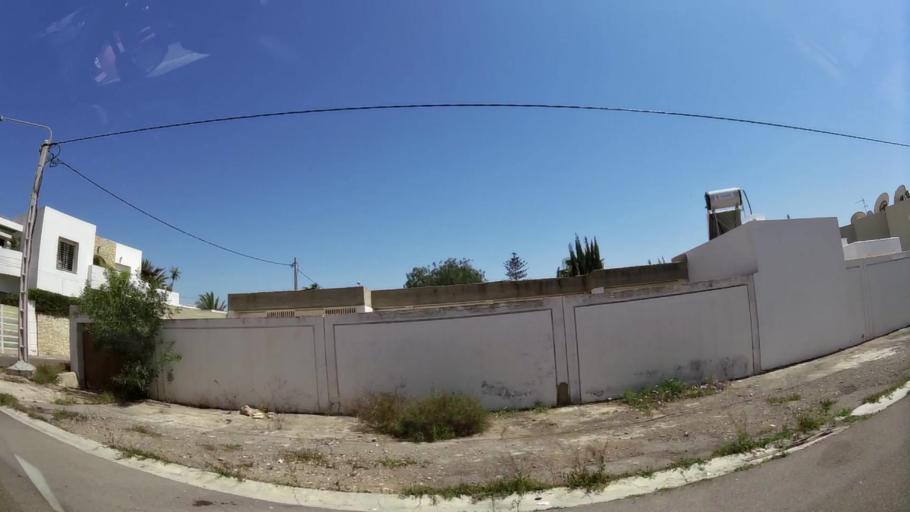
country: MA
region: Souss-Massa-Draa
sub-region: Agadir-Ida-ou-Tnan
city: Agadir
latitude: 30.4256
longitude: -9.6033
